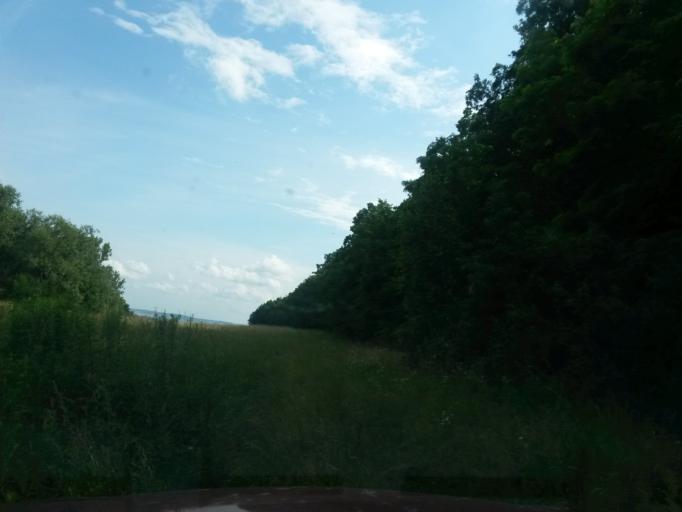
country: SK
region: Kosicky
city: Moldava nad Bodvou
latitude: 48.6214
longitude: 21.0988
